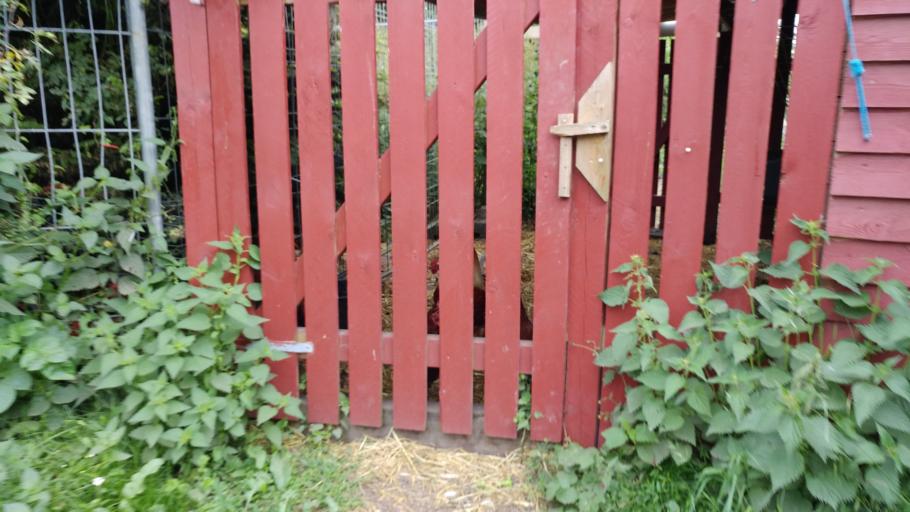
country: DK
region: South Denmark
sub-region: Nordfyns Kommune
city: Otterup
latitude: 55.5680
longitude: 10.4273
